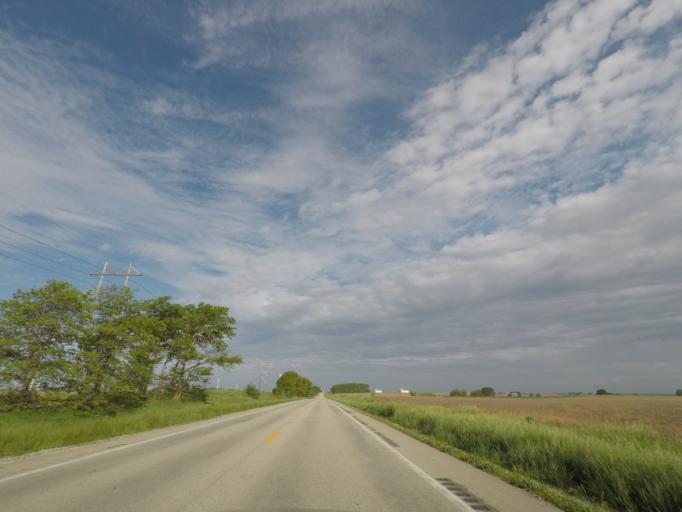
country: US
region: Illinois
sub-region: Logan County
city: Mount Pulaski
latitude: 39.9778
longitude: -89.1999
